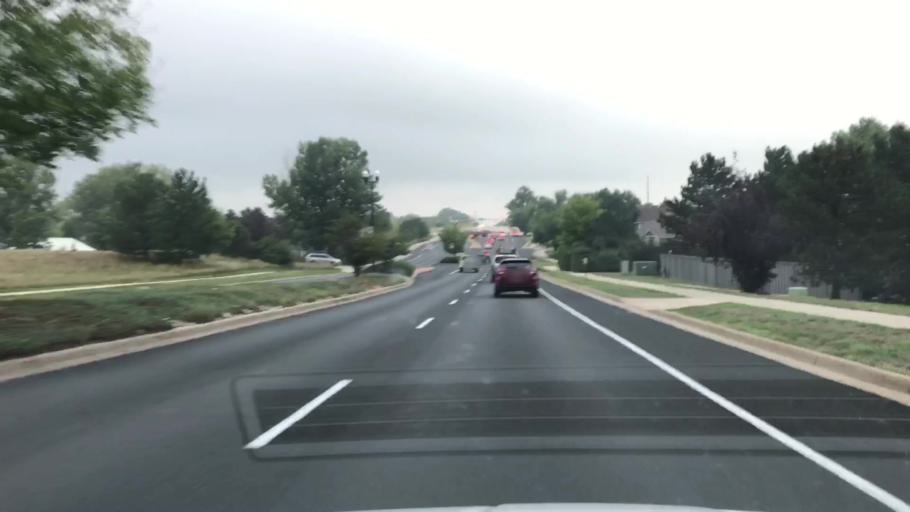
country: US
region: Colorado
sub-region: Boulder County
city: Louisville
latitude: 40.0003
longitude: -105.1265
